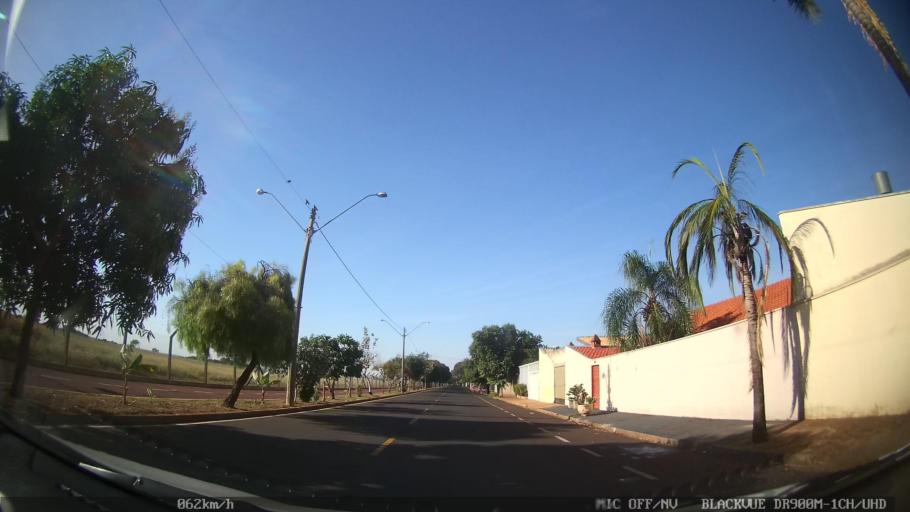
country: BR
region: Sao Paulo
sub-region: Sao Jose Do Rio Preto
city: Sao Jose do Rio Preto
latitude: -20.8198
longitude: -49.4084
